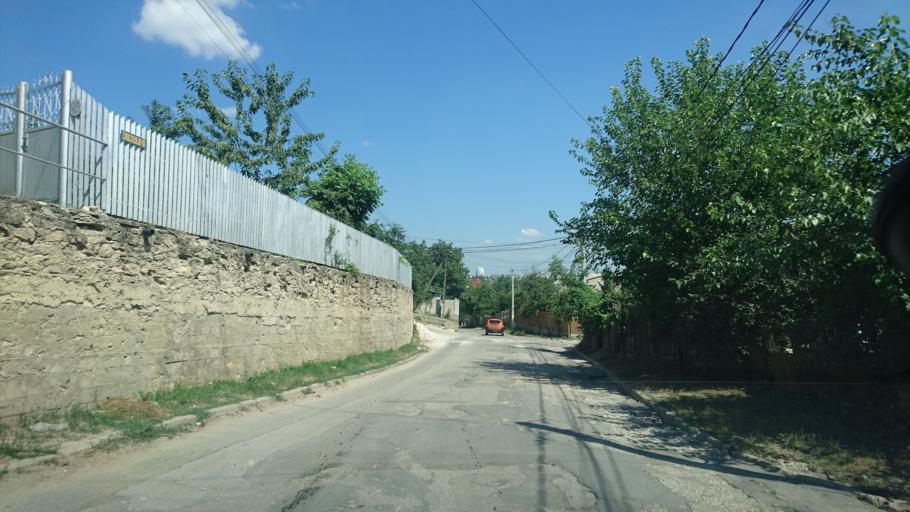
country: MD
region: Chisinau
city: Vatra
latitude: 47.0132
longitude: 28.7670
